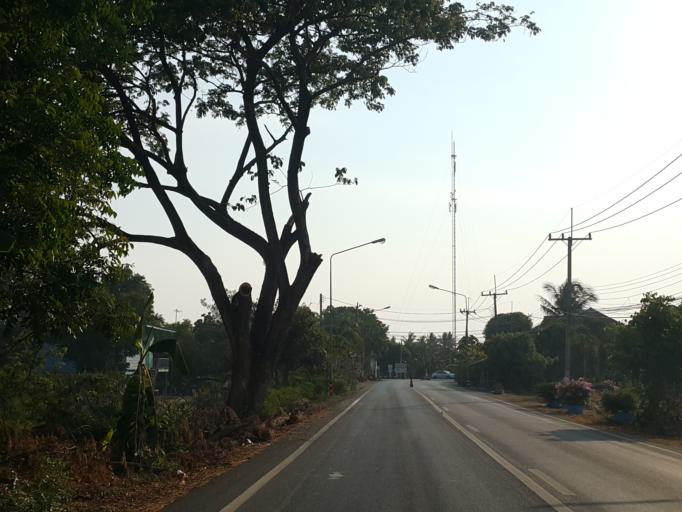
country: TH
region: Uttaradit
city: Phichai
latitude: 17.1641
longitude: 100.0996
